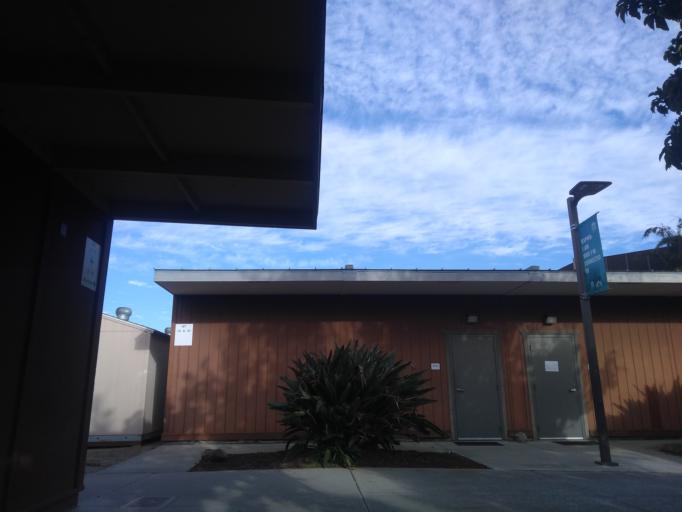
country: US
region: California
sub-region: Santa Clara County
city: Santa Clara
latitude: 37.3906
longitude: -121.9830
